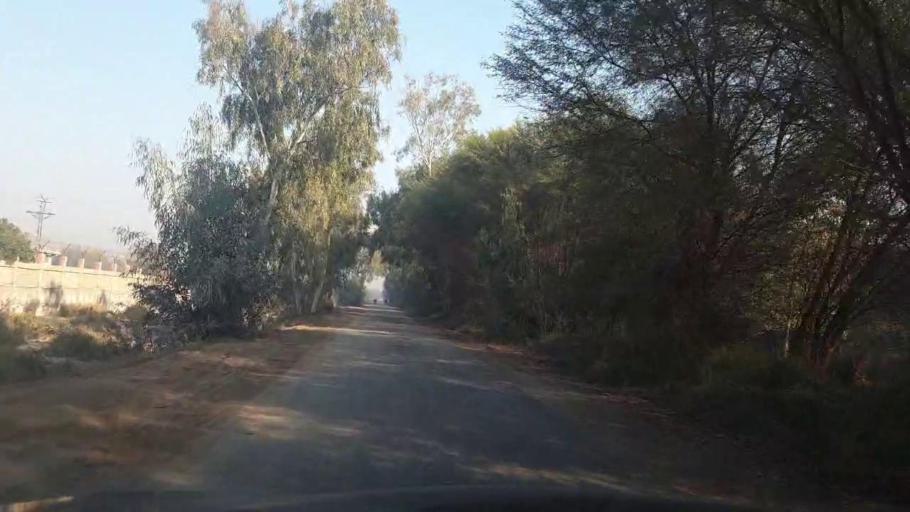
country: PK
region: Sindh
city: Mirpur Mathelo
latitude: 28.0490
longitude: 69.4603
